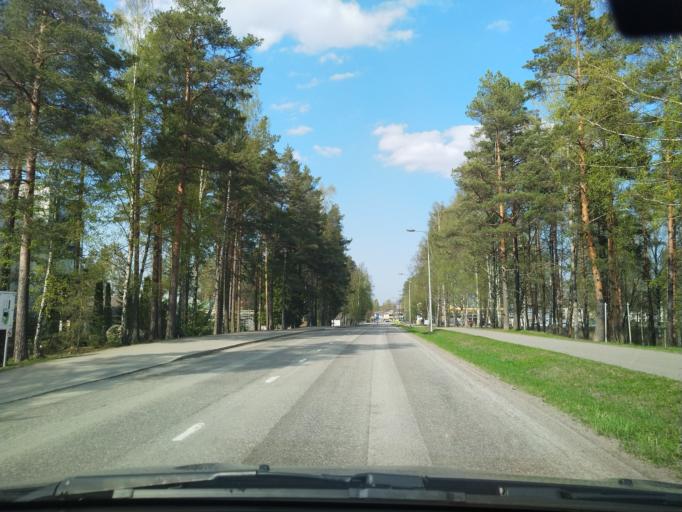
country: FI
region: Uusimaa
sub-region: Helsinki
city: Lohja
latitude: 60.1865
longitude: 23.9958
